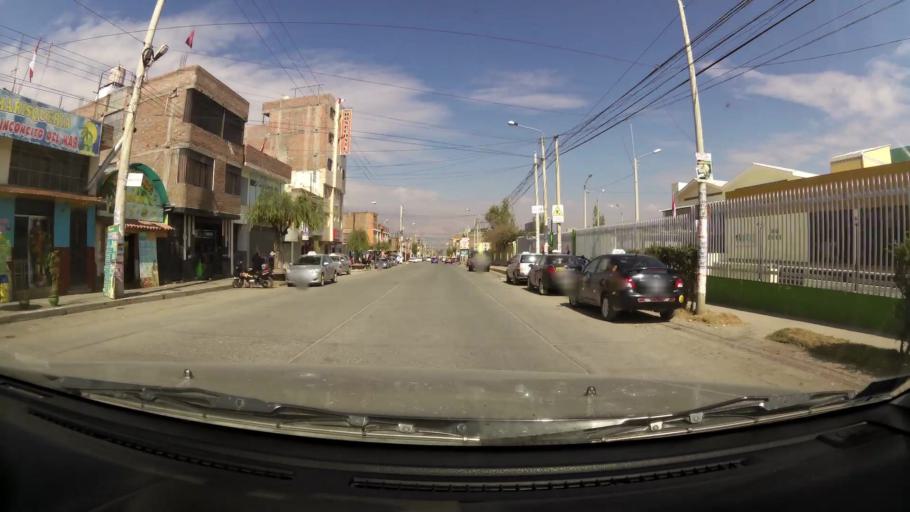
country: PE
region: Junin
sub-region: Provincia de Huancayo
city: El Tambo
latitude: -12.0737
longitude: -75.2214
